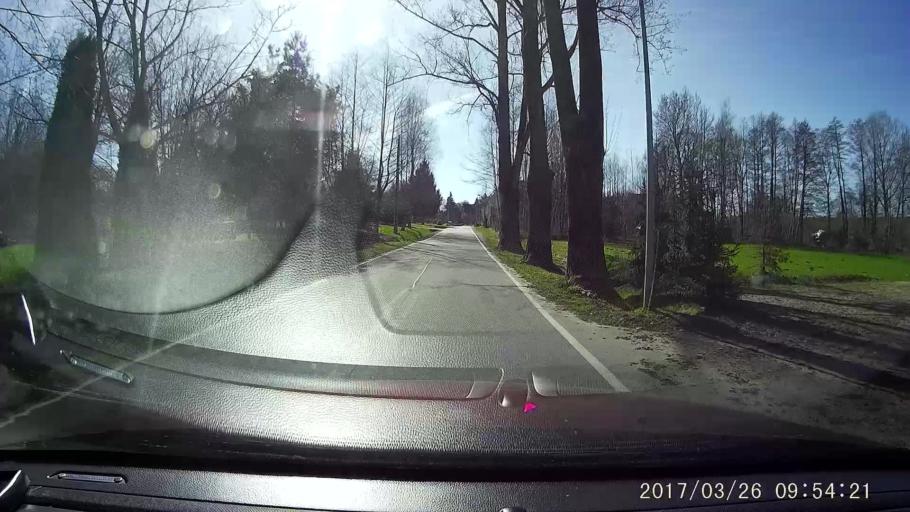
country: DE
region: Saxony
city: Sohland am Rotstein
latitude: 51.0990
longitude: 14.7403
